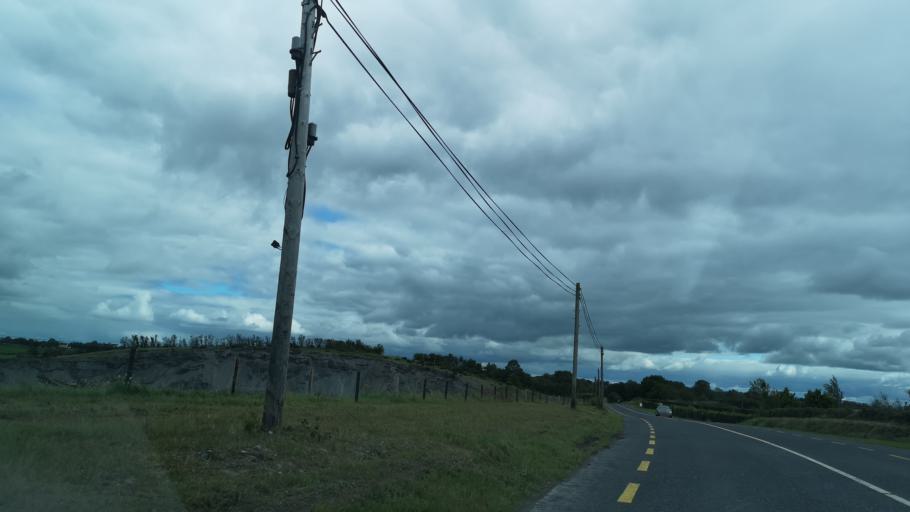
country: IE
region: Connaught
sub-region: County Galway
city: Ballinasloe
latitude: 53.3046
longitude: -8.1397
